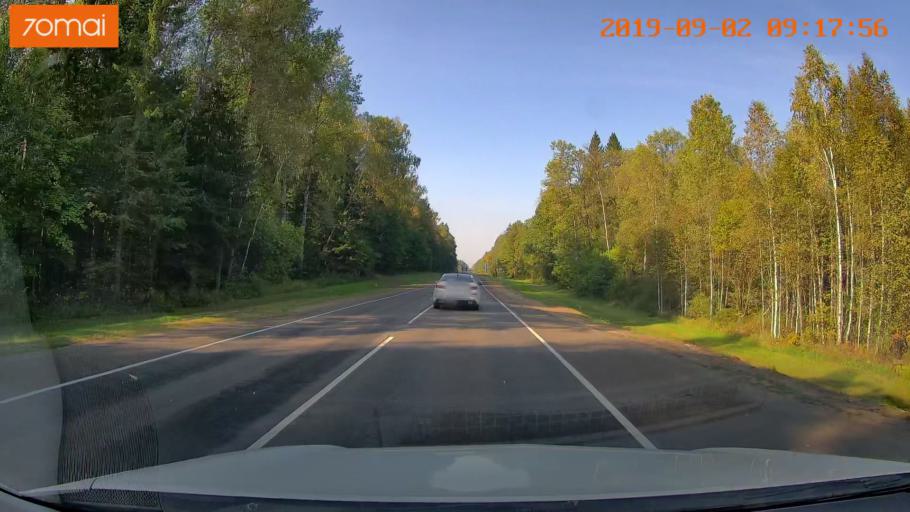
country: RU
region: Kaluga
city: Nikola-Lenivets
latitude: 54.8202
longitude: 35.4401
